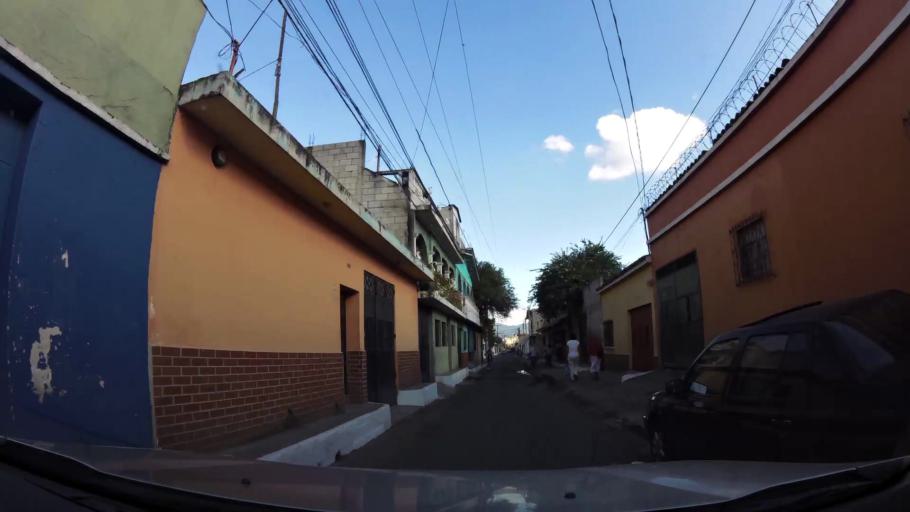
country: GT
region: Guatemala
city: Villa Nueva
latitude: 14.5217
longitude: -90.5822
